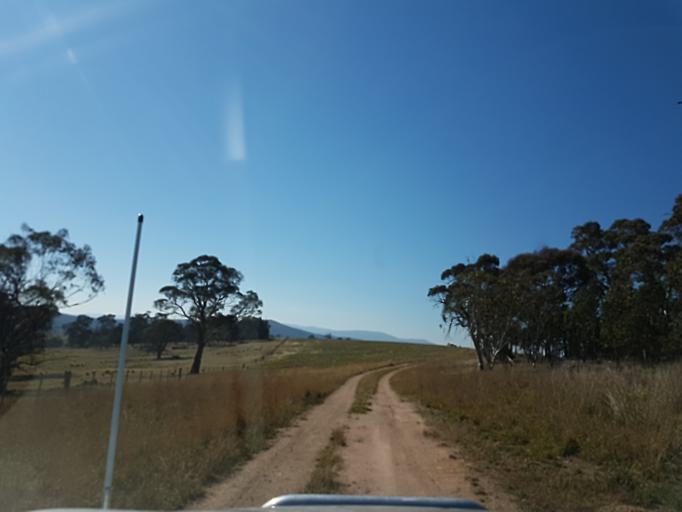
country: AU
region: New South Wales
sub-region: Snowy River
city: Jindabyne
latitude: -37.0428
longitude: 148.2846
